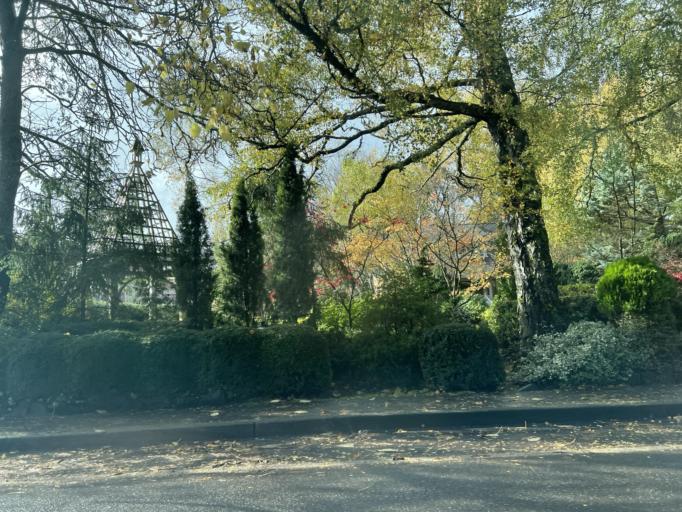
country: US
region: Washington
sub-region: Kitsap County
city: Bainbridge Island
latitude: 47.6331
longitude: -122.5210
